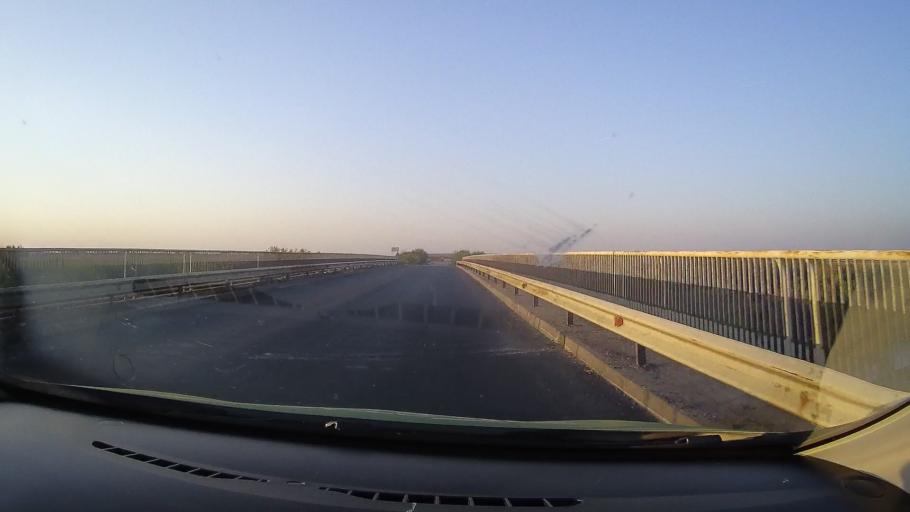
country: RO
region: Arad
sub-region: Comuna Ineu
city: Ineu
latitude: 46.4316
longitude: 21.8595
